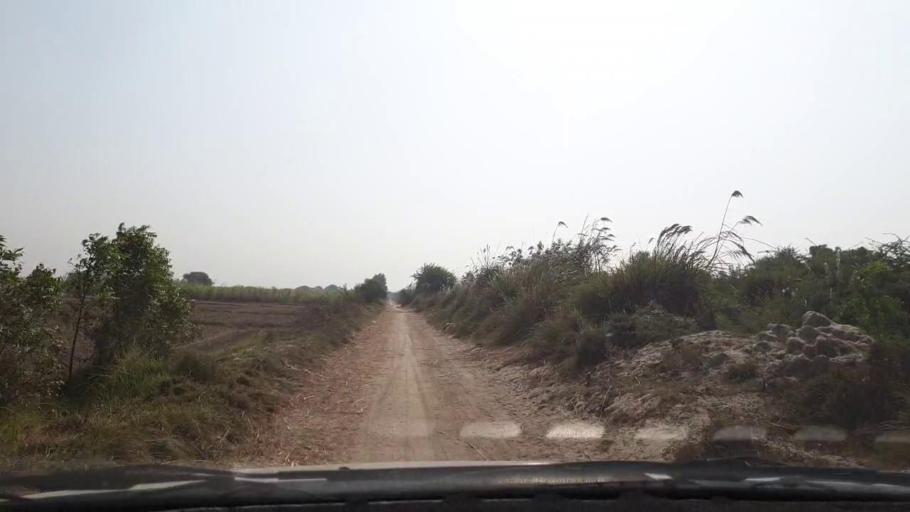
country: PK
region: Sindh
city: Tando Muhammad Khan
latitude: 25.0859
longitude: 68.3589
